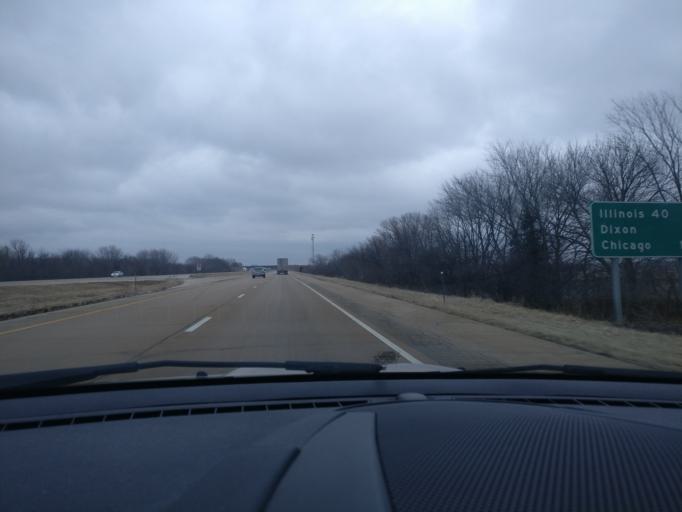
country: US
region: Illinois
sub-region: Whiteside County
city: Sterling
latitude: 41.7546
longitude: -89.7671
